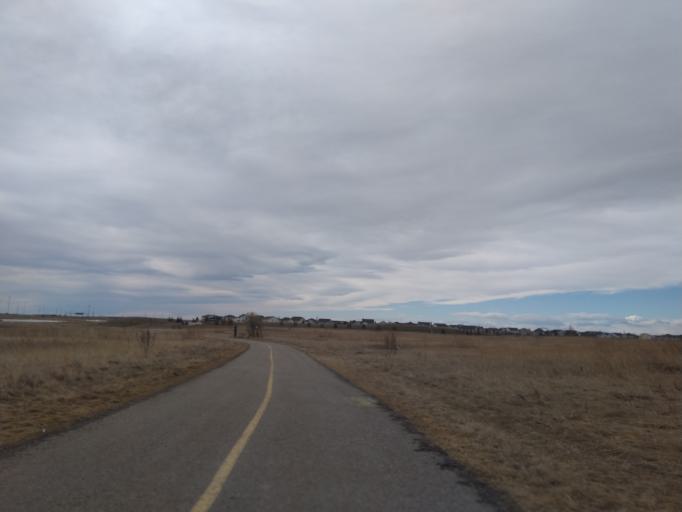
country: CA
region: Alberta
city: Chestermere
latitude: 51.1137
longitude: -113.9238
